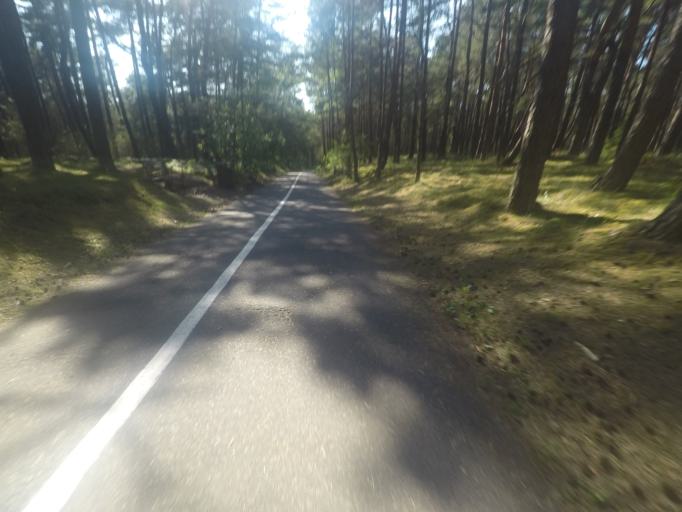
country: LT
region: Klaipedos apskritis
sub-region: Klaipeda
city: Klaipeda
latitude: 55.5470
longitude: 21.1097
